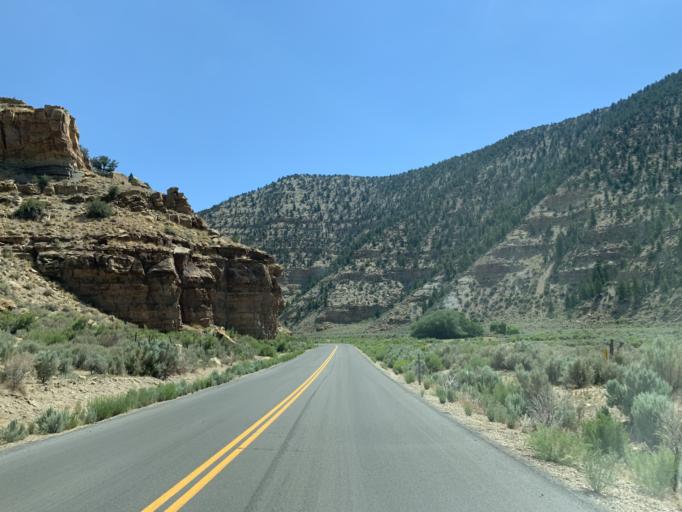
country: US
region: Utah
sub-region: Carbon County
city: East Carbon City
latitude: 39.7854
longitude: -110.3990
